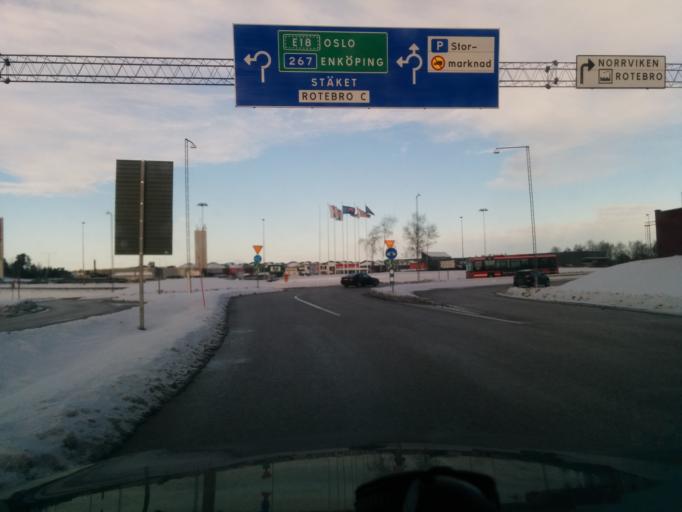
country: SE
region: Stockholm
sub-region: Upplands Vasby Kommun
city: Upplands Vaesby
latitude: 59.4690
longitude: 17.9152
